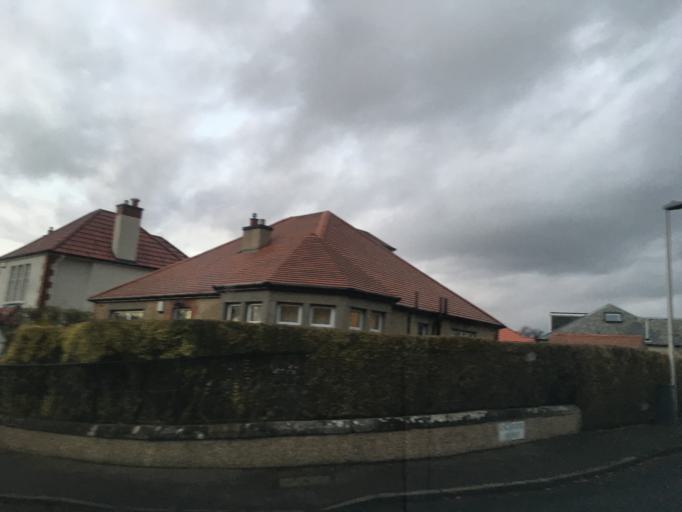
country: GB
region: Scotland
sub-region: Edinburgh
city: Colinton
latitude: 55.9159
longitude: -3.2640
